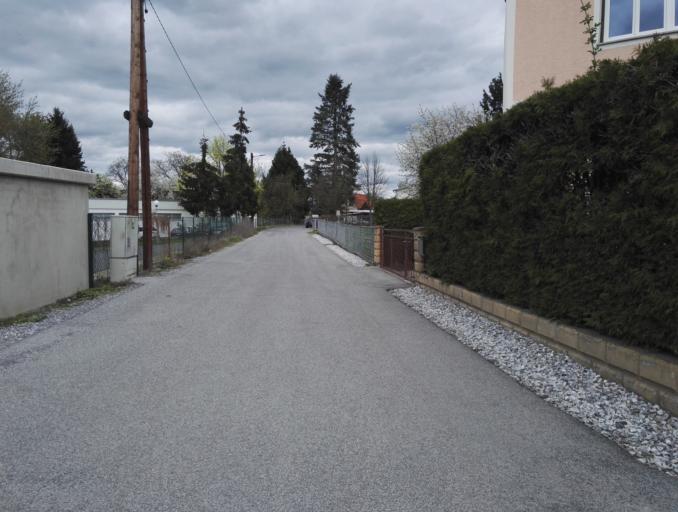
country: AT
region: Styria
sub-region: Politischer Bezirk Graz-Umgebung
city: Feldkirchen bei Graz
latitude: 47.0349
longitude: 15.4635
